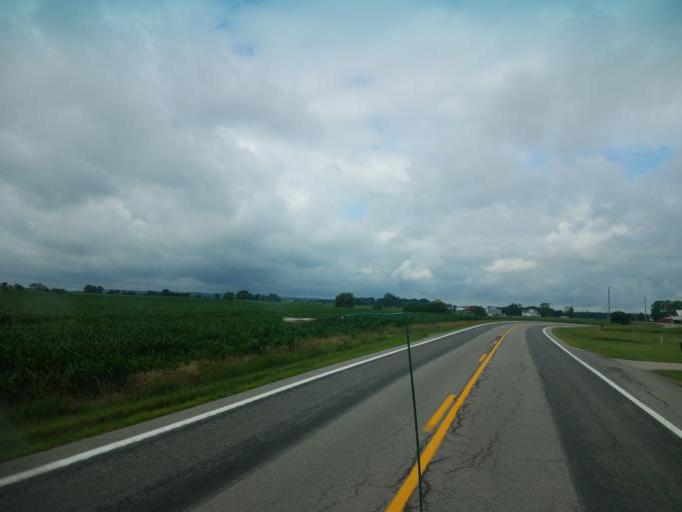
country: US
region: Ohio
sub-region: Champaign County
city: North Lewisburg
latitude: 40.4067
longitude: -83.5576
